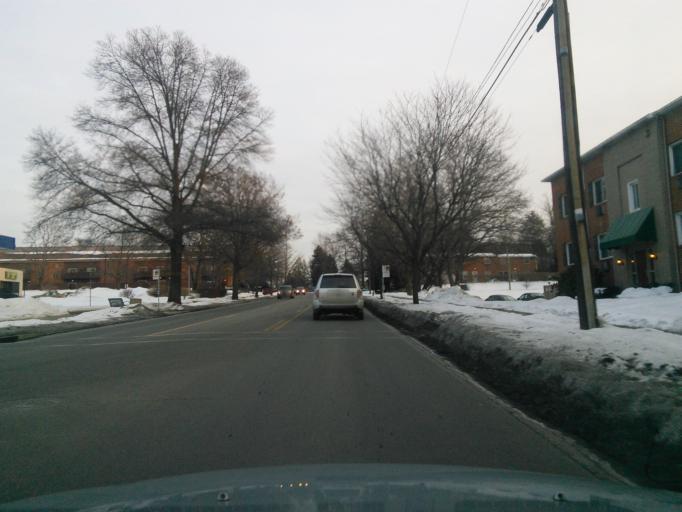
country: US
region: Pennsylvania
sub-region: Centre County
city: State College
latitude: 40.7993
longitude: -77.8479
